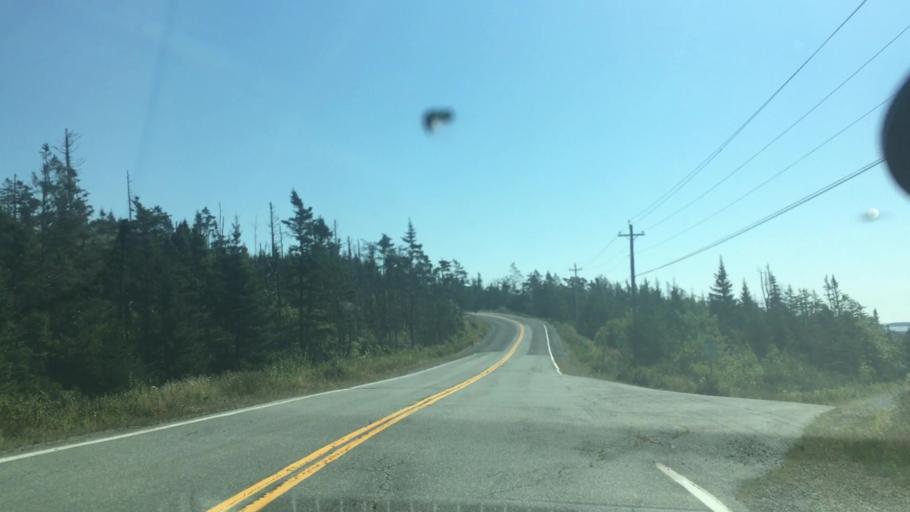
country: CA
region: Nova Scotia
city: New Glasgow
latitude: 44.9168
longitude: -62.3202
